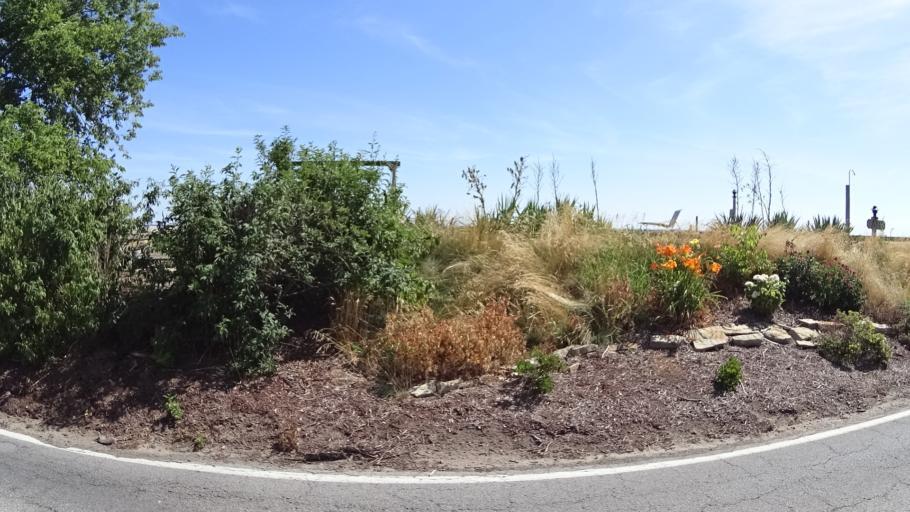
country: US
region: Ohio
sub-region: Erie County
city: Sandusky
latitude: 41.4476
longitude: -82.6422
